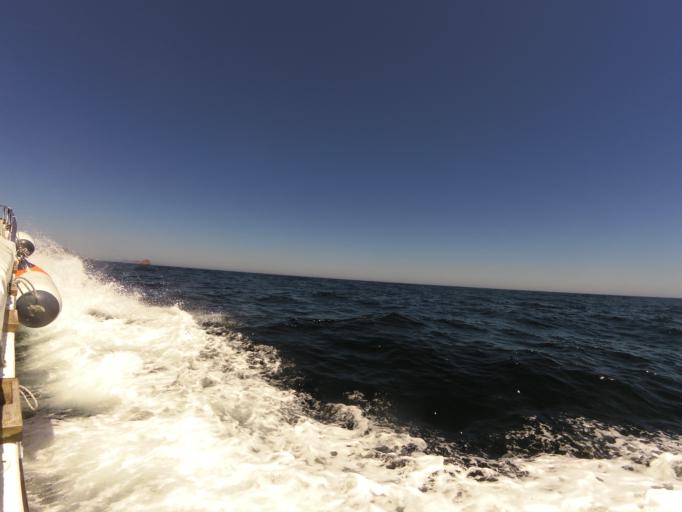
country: PT
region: Leiria
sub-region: Peniche
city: Peniche
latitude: 39.3952
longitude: -9.4798
